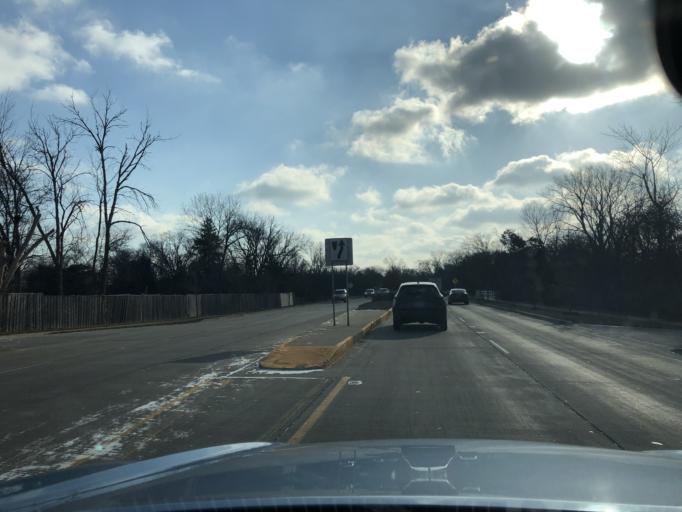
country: US
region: Illinois
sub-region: Cook County
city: Northfield
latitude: 42.1041
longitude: -87.7850
